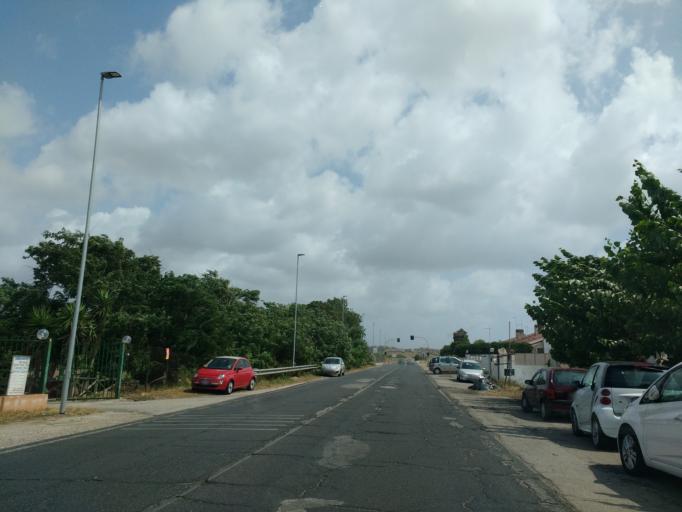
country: IT
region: Latium
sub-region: Citta metropolitana di Roma Capitale
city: Marina di Ardea-Tor San Lorenzo
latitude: 41.5613
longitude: 12.5300
